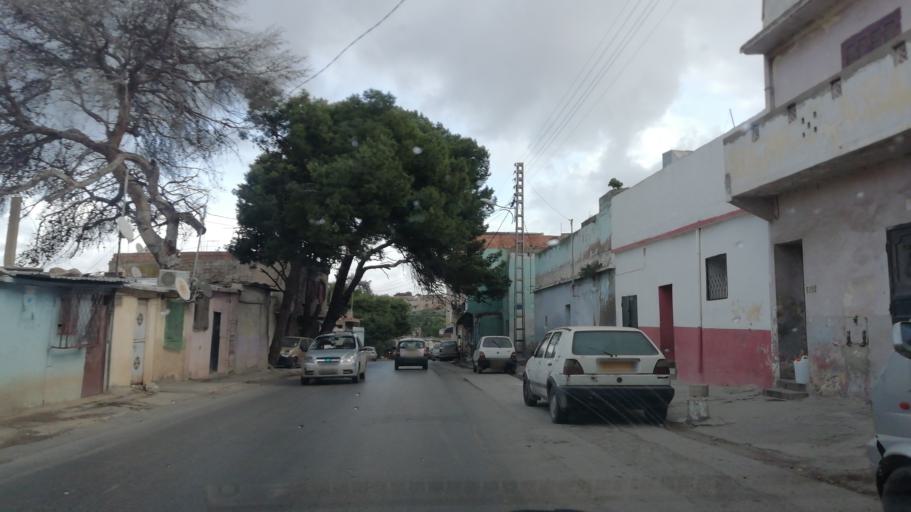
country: DZ
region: Oran
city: Oran
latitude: 35.6963
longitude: -0.6609
